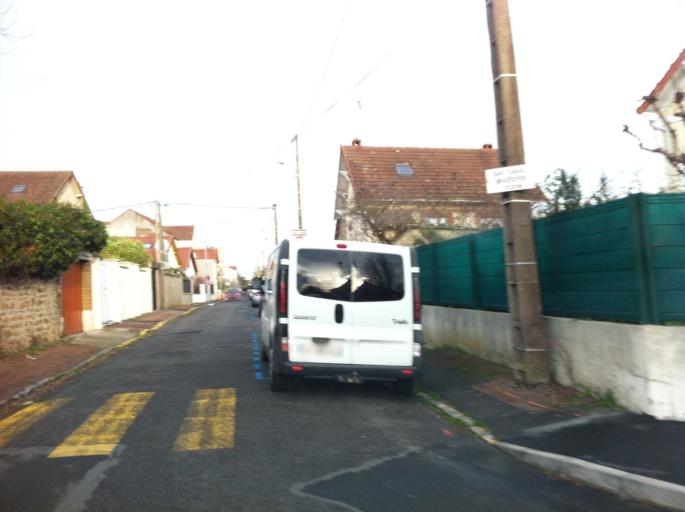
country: FR
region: Ile-de-France
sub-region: Departement de Seine-et-Marne
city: Dammarie-les-Lys
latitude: 48.5307
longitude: 2.6451
